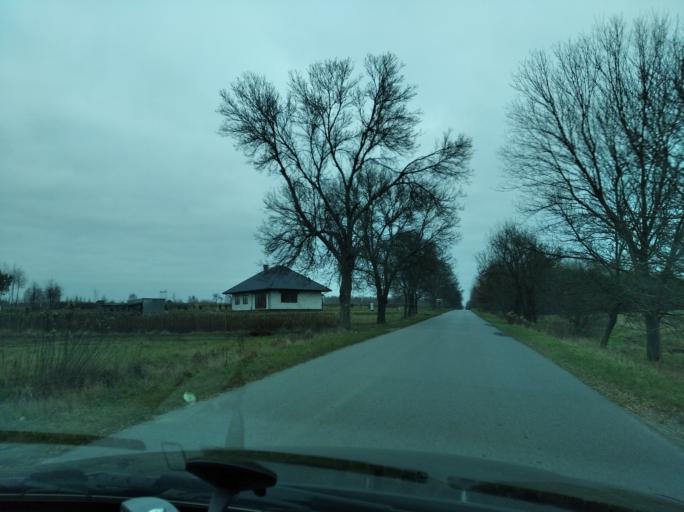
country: PL
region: Subcarpathian Voivodeship
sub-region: Powiat lancucki
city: Rakszawa
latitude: 50.1766
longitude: 22.2395
